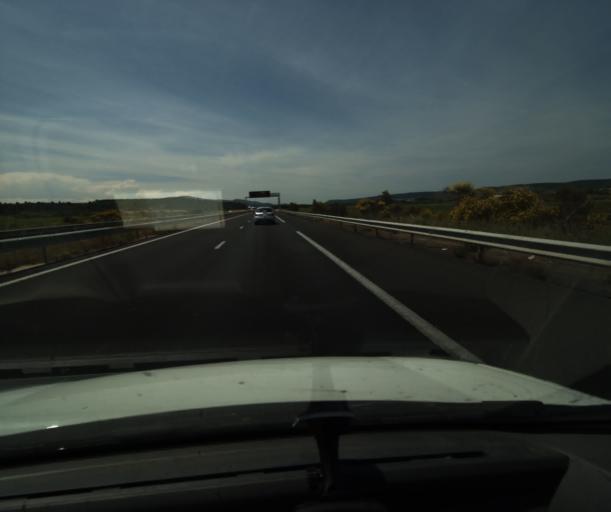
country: FR
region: Languedoc-Roussillon
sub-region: Departement de l'Aude
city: Lezignan-Corbieres
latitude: 43.1704
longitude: 2.7785
